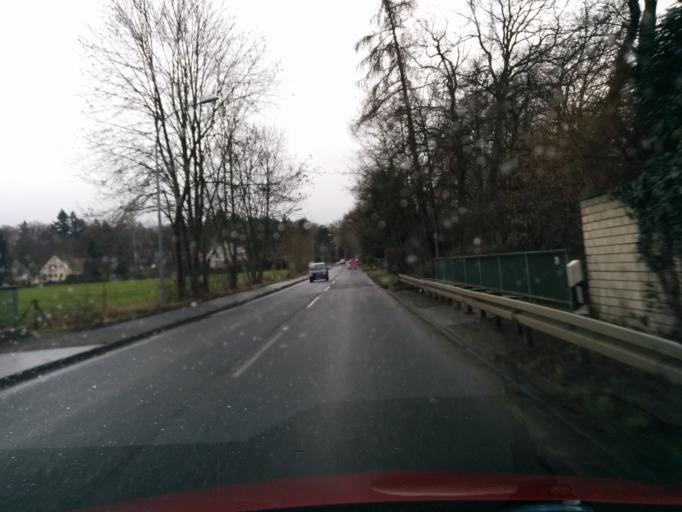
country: DE
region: North Rhine-Westphalia
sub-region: Regierungsbezirk Koln
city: Rheinbach
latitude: 50.6130
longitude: 6.9443
